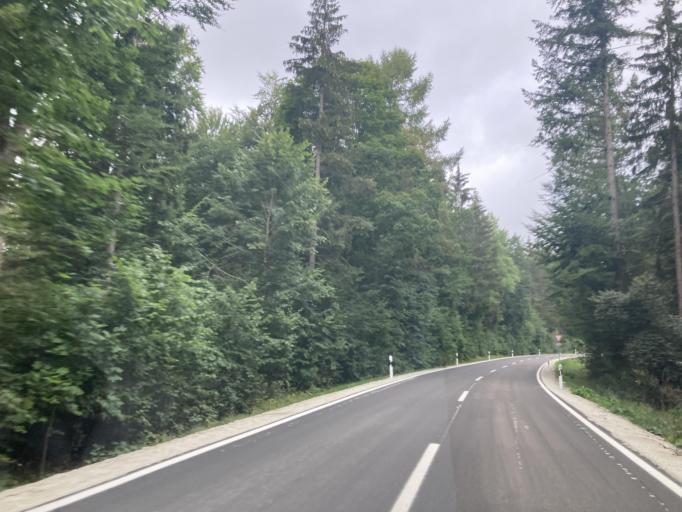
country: DE
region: Bavaria
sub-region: Swabia
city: Forheim
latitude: 48.8032
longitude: 10.4104
